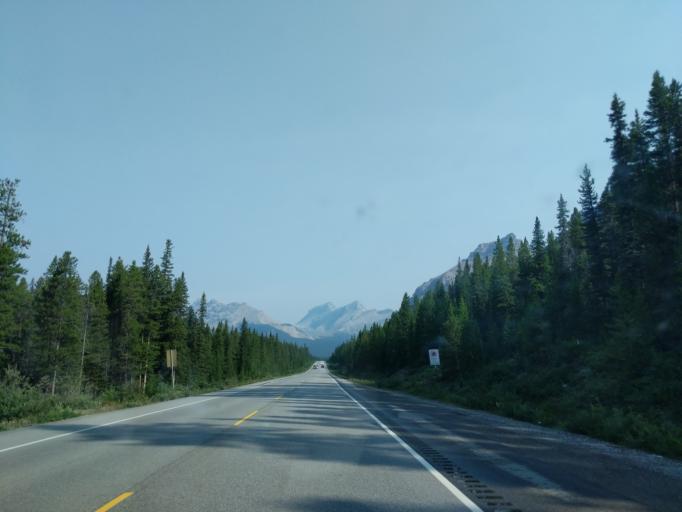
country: CA
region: Alberta
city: Lake Louise
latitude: 51.6028
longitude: -116.3099
